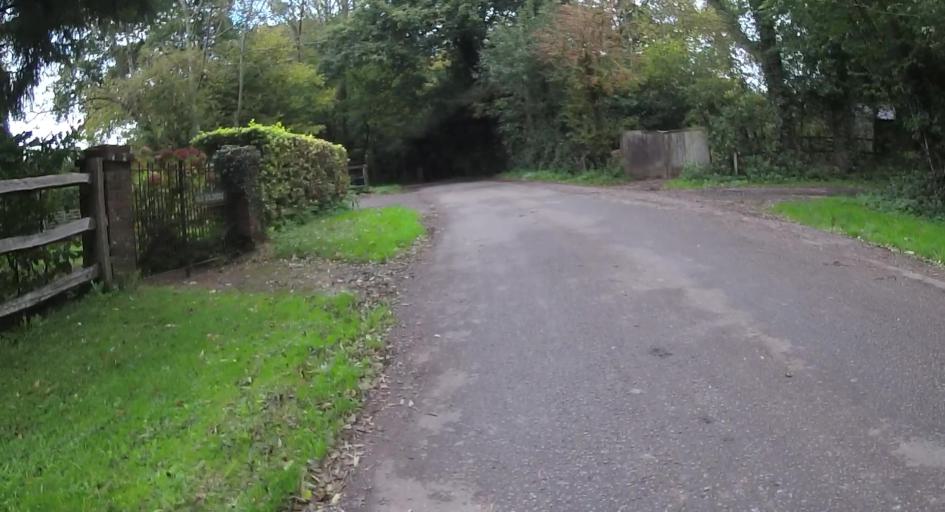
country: GB
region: England
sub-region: Hampshire
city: Four Marks
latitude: 51.1101
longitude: -1.0735
